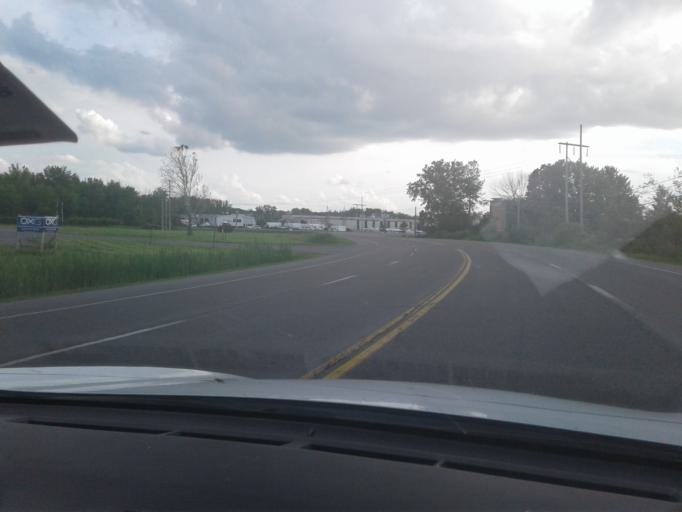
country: US
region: New York
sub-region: Onondaga County
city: East Syracuse
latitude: 43.0933
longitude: -76.0683
